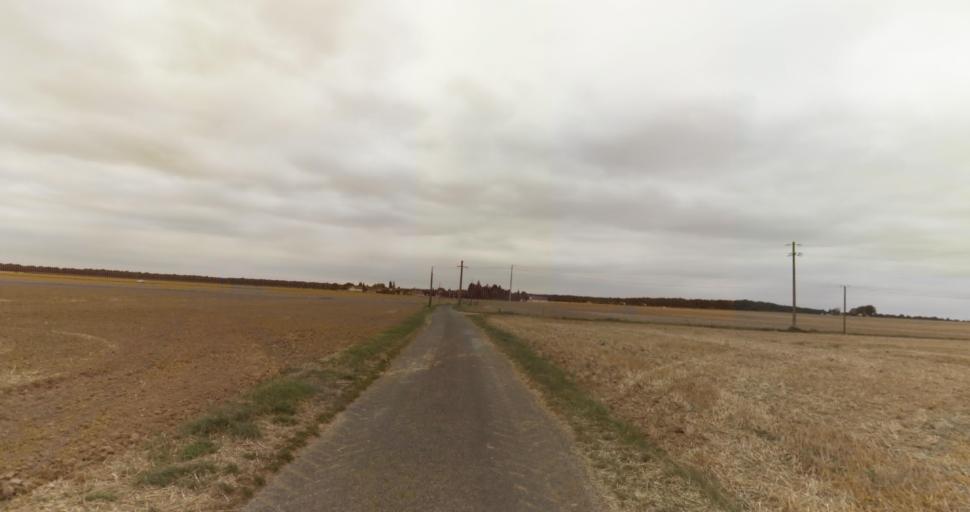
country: FR
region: Haute-Normandie
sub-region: Departement de l'Eure
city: La Couture-Boussey
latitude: 48.9153
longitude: 1.3167
